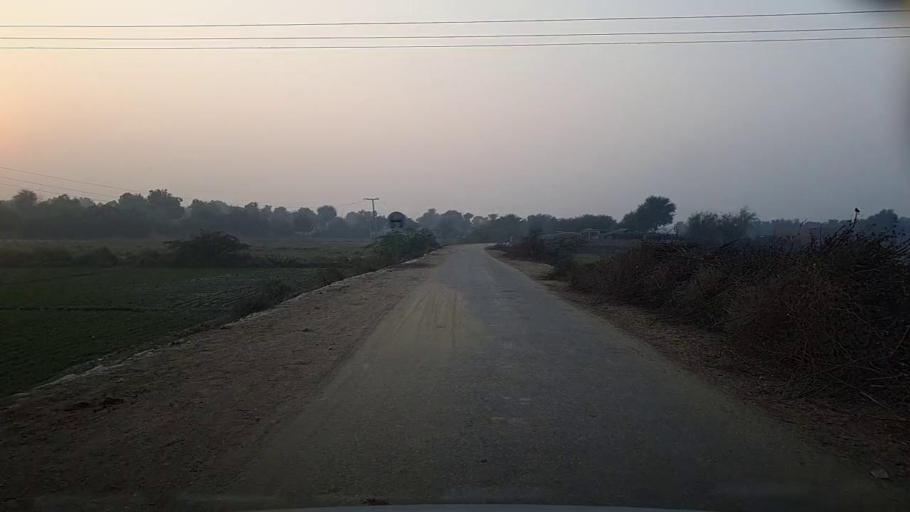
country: PK
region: Sindh
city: Bozdar
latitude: 27.0562
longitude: 68.5991
